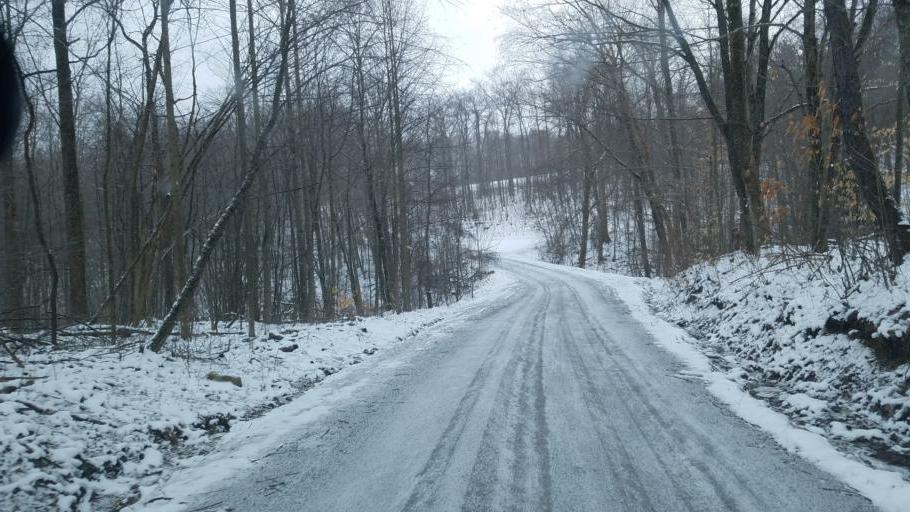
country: US
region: Pennsylvania
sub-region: Venango County
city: Sugarcreek
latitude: 41.4387
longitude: -79.9809
